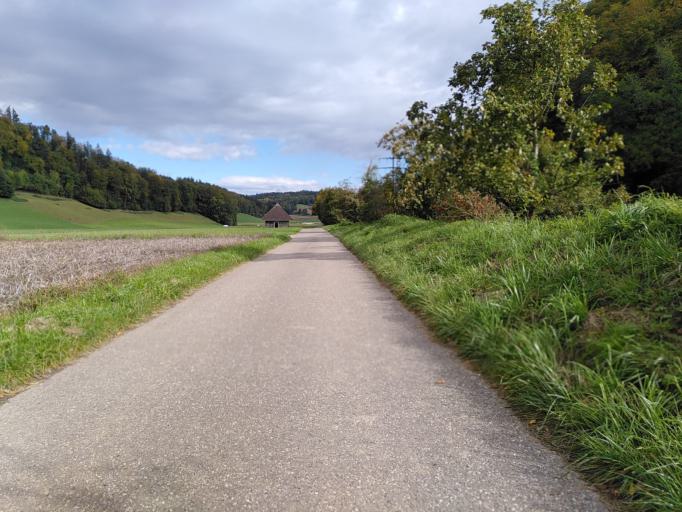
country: CH
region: Bern
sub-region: Emmental District
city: Wynigen
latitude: 47.1170
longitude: 7.6690
